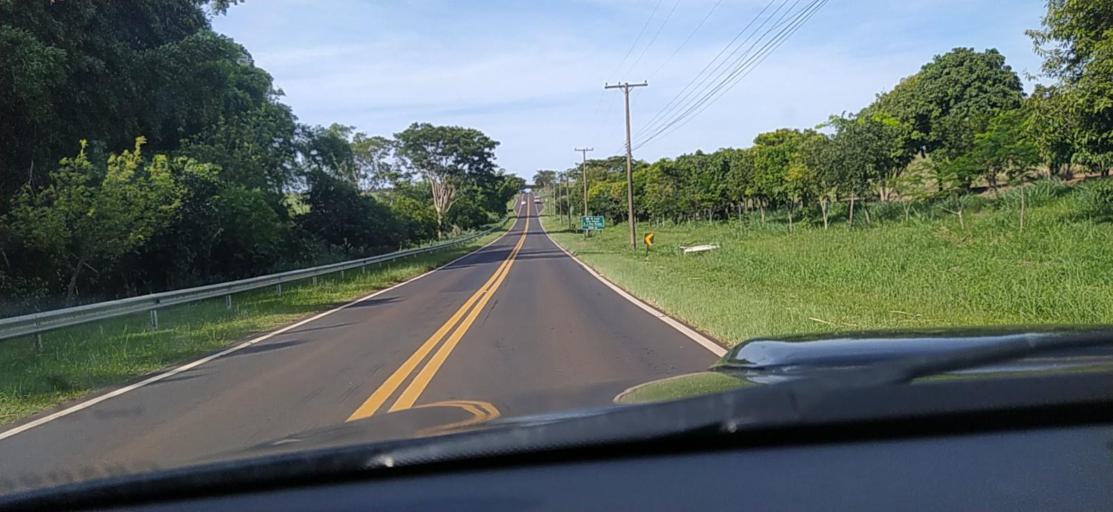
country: BR
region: Sao Paulo
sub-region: Pindorama
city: Pindorama
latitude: -21.2032
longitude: -48.9273
